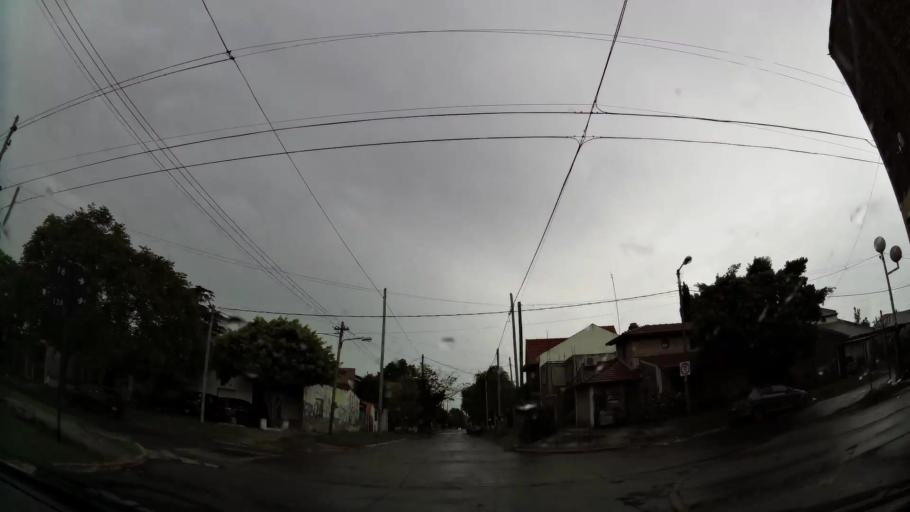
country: AR
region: Buenos Aires
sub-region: Partido de Quilmes
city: Quilmes
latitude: -34.7723
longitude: -58.2193
